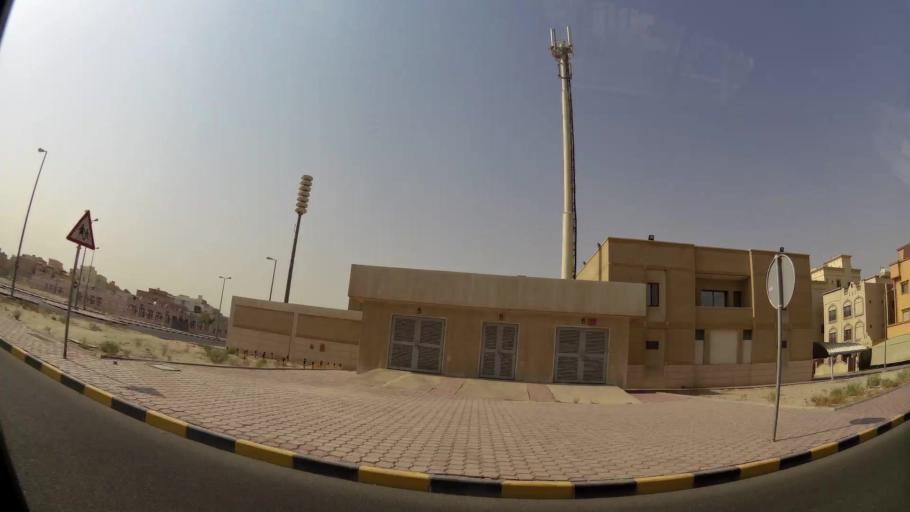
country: KW
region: Muhafazat al Jahra'
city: Al Jahra'
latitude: 29.3311
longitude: 47.7751
